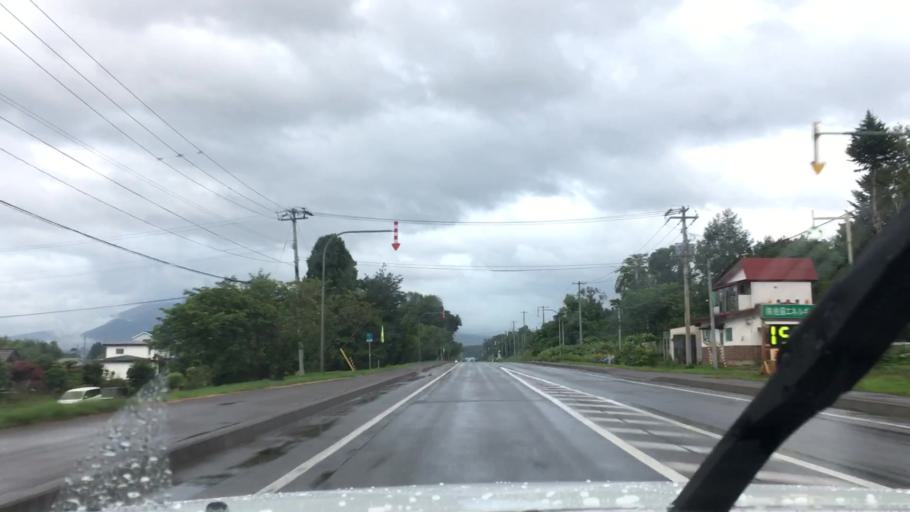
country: JP
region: Hokkaido
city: Nanae
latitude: 42.1111
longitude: 140.5493
